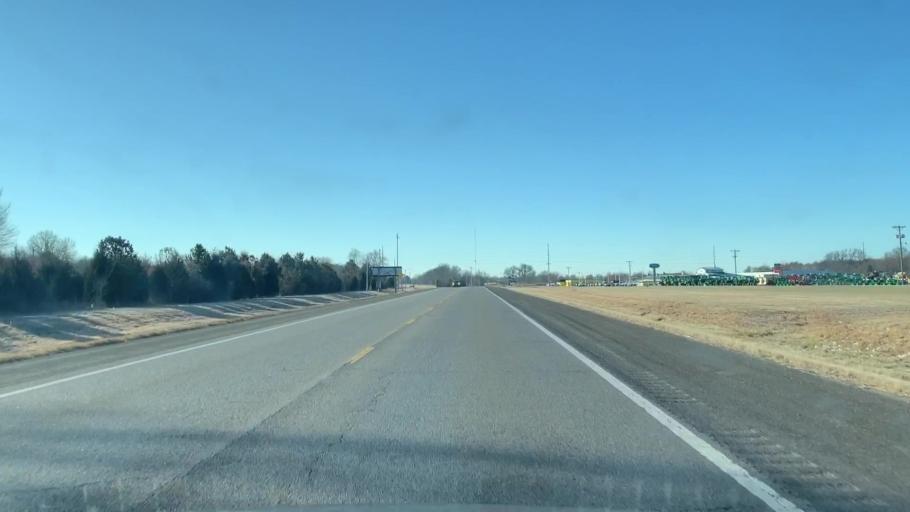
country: US
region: Kansas
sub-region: Crawford County
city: Pittsburg
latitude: 37.3712
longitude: -94.7088
